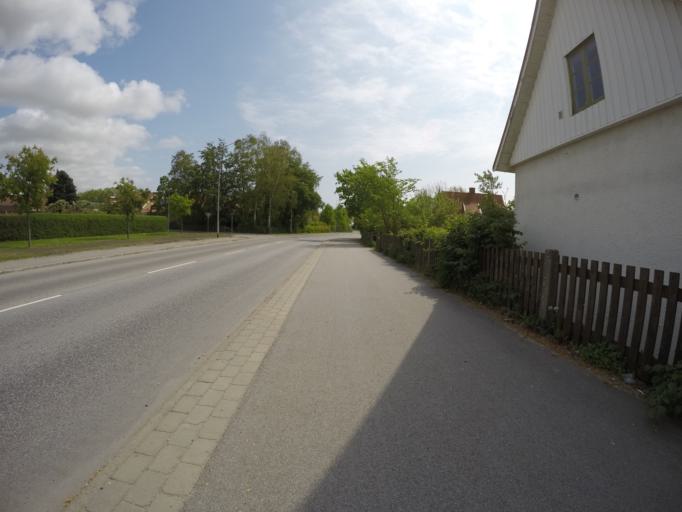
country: SE
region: Skane
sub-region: Malmo
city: Tygelsjo
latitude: 55.5191
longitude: 12.9983
